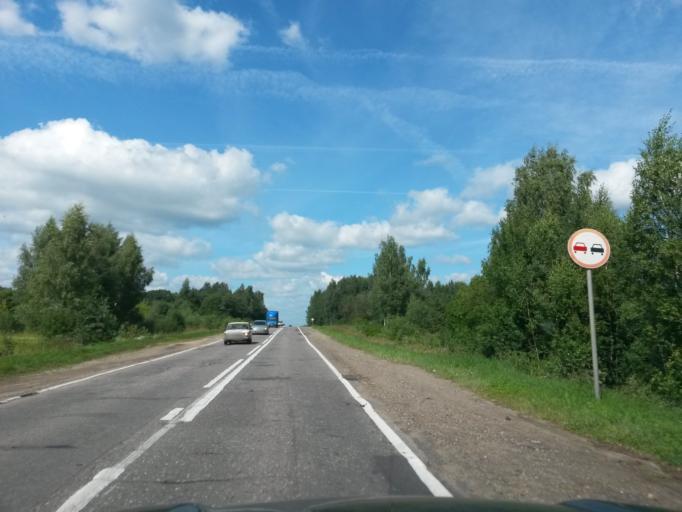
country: RU
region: Jaroslavl
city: Krasnyye Tkachi
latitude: 57.4794
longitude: 39.9056
